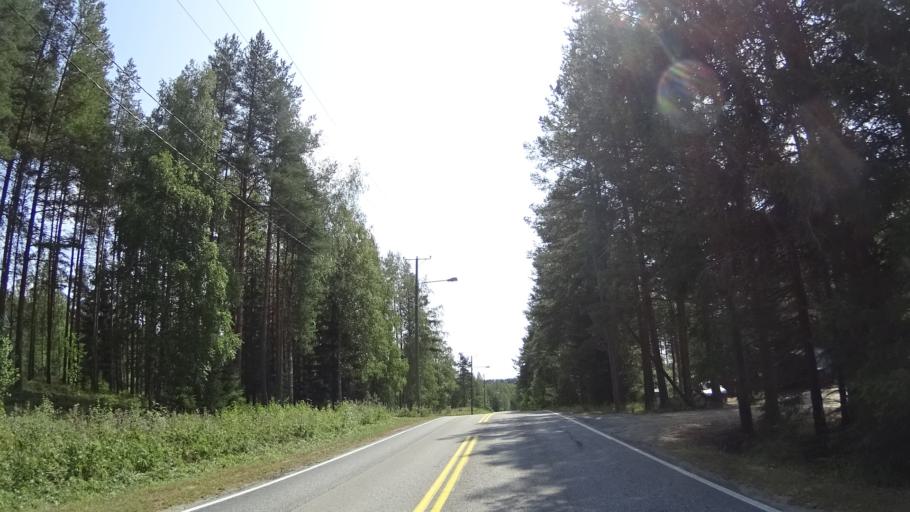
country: FI
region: Pirkanmaa
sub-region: Ylae-Pirkanmaa
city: Maenttae
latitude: 61.9013
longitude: 24.7913
